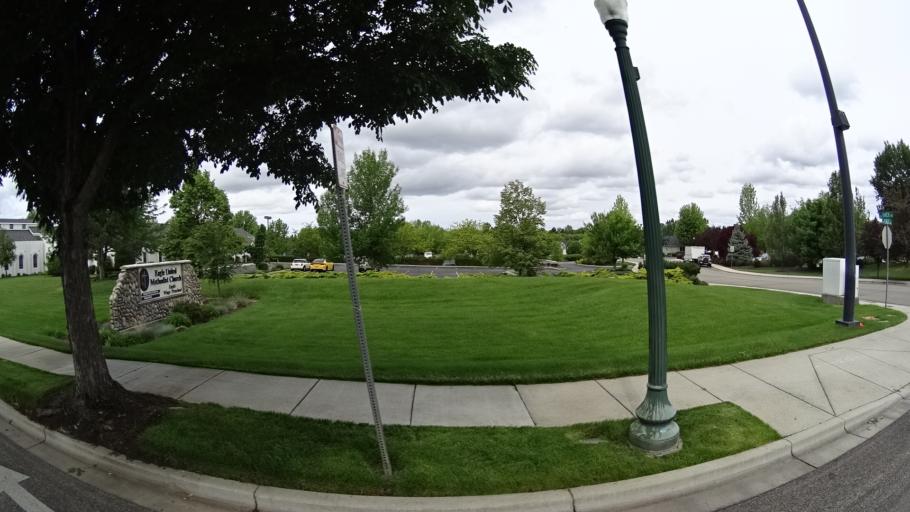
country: US
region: Idaho
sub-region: Ada County
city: Eagle
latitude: 43.7016
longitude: -116.3540
